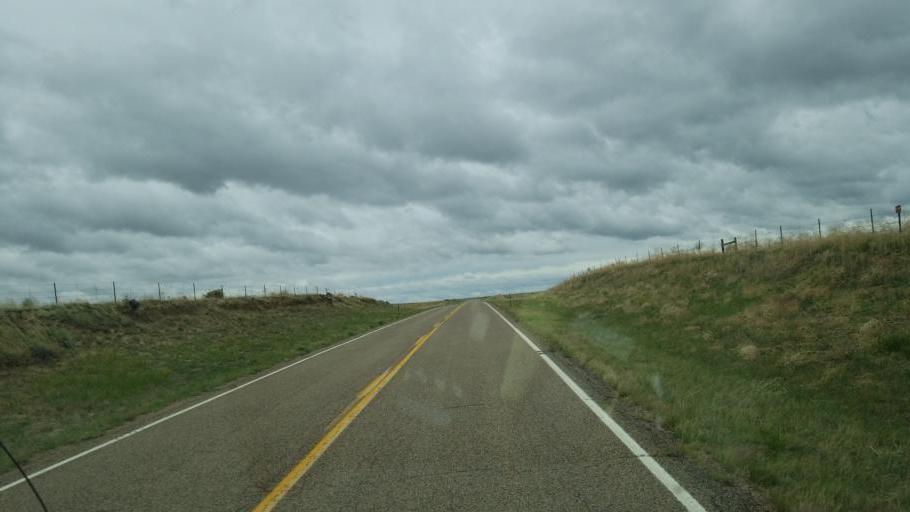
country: US
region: Colorado
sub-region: Lincoln County
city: Hugo
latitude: 38.8508
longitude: -103.5820
